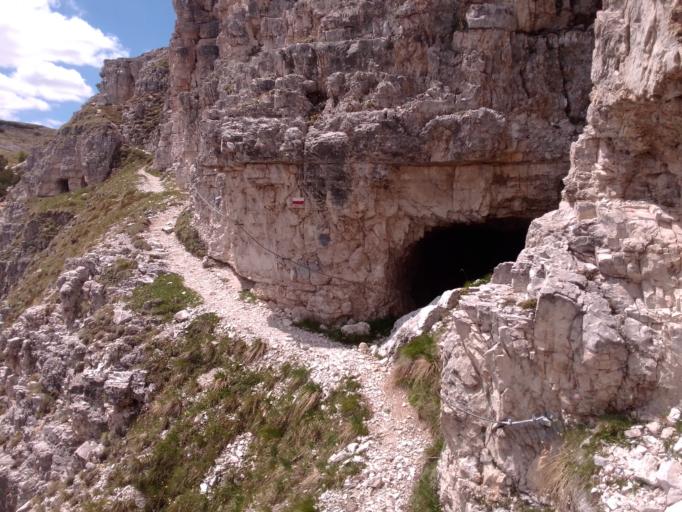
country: IT
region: Trentino-Alto Adige
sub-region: Bolzano
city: Dobbiaco
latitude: 46.6201
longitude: 12.2479
